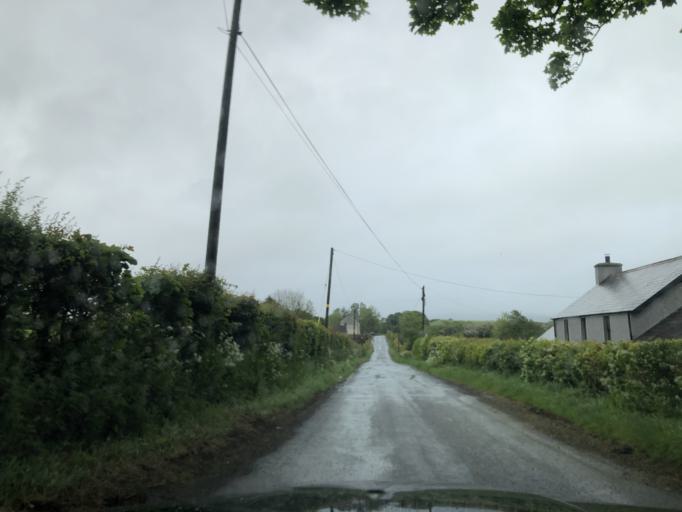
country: GB
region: Northern Ireland
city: Dunloy
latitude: 55.1331
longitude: -6.3709
